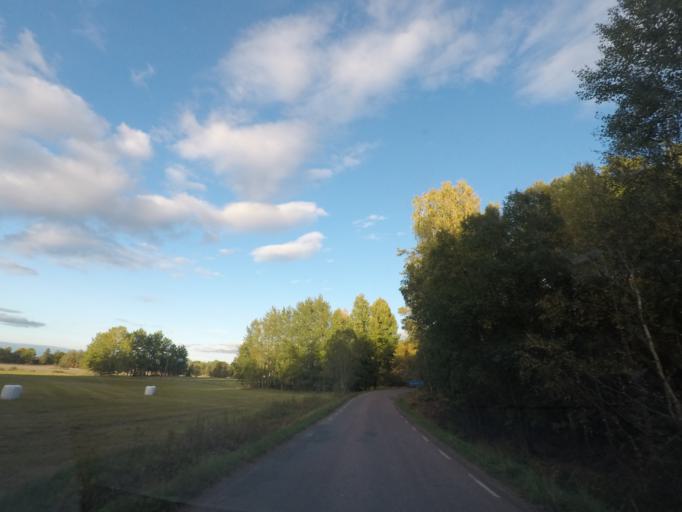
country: SE
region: Vaestmanland
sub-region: Kungsors Kommun
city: Kungsoer
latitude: 59.5078
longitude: 16.0973
